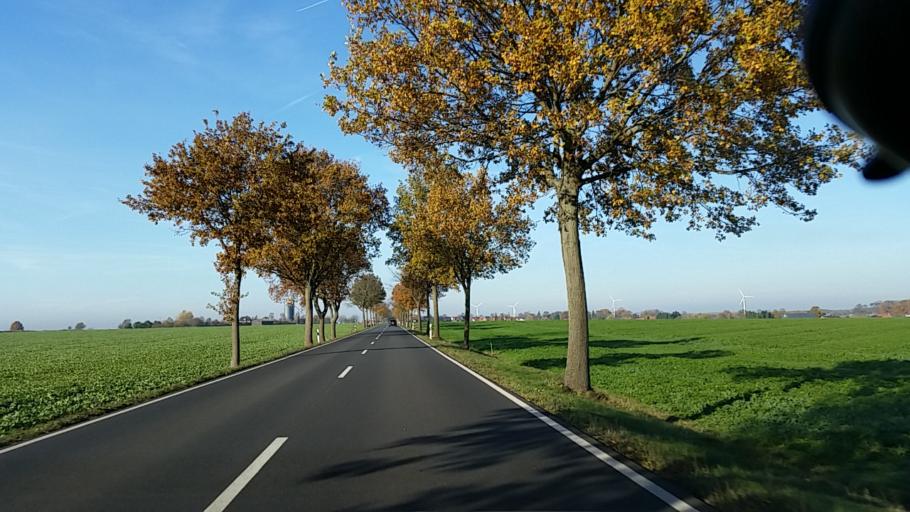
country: DE
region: Lower Saxony
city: Wittingen
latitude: 52.6878
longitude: 10.8196
